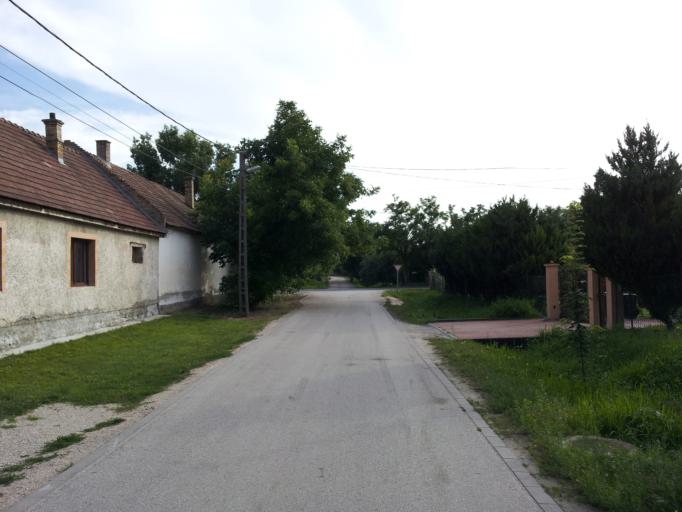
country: HU
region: Pest
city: Kiskunlachaza
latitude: 47.1878
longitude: 19.0131
